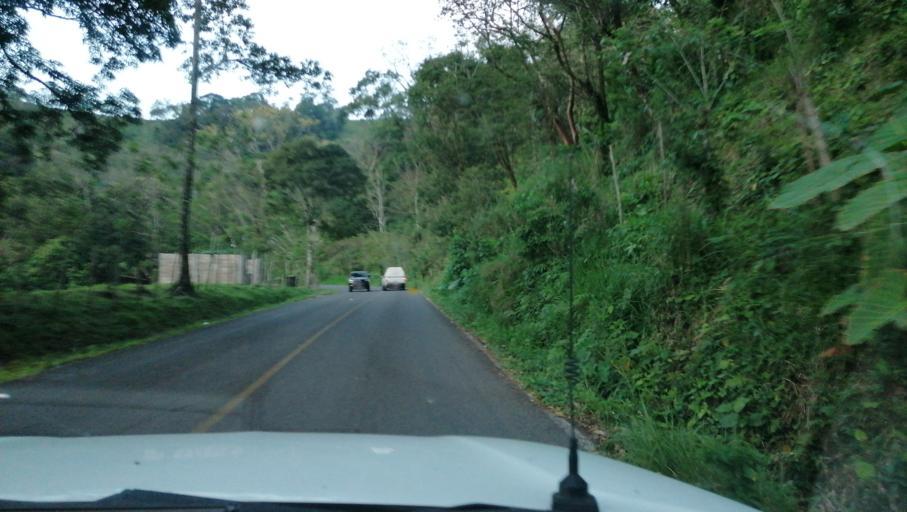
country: MX
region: Chiapas
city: Ostuacan
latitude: 17.4241
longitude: -93.3455
